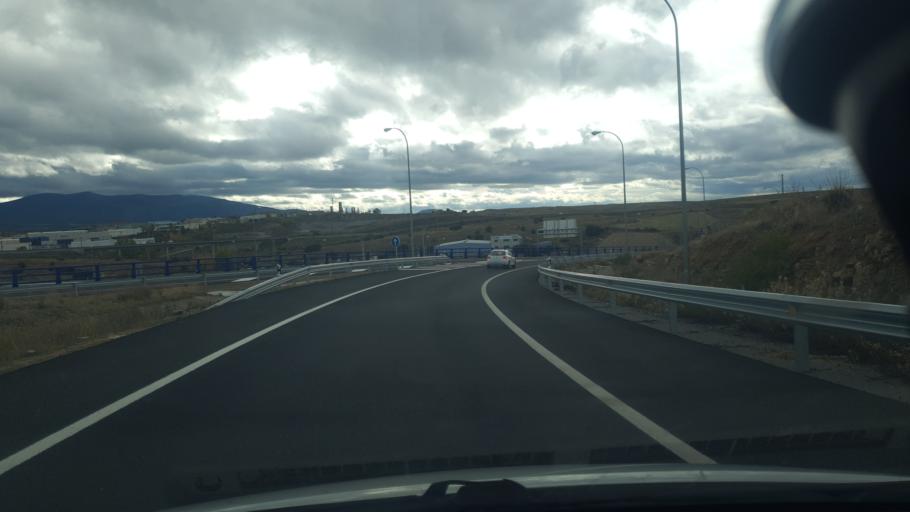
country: ES
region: Castille and Leon
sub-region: Provincia de Segovia
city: Segovia
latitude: 40.9204
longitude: -4.1099
